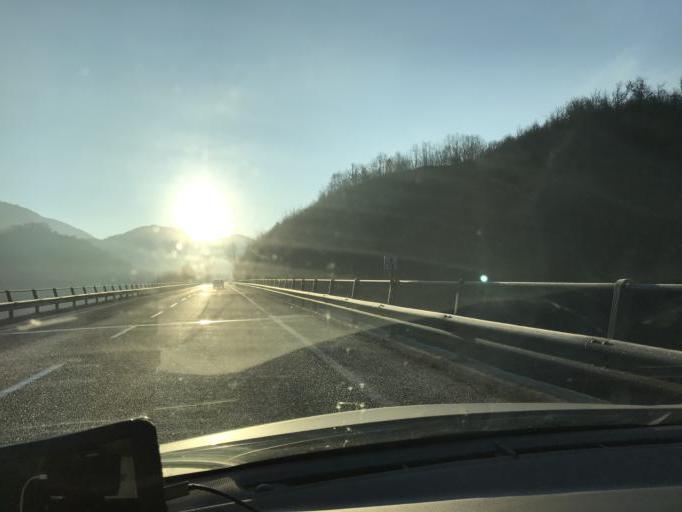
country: IT
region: Latium
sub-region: Provincia di Rieti
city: Concerviano
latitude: 42.3303
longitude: 13.0141
